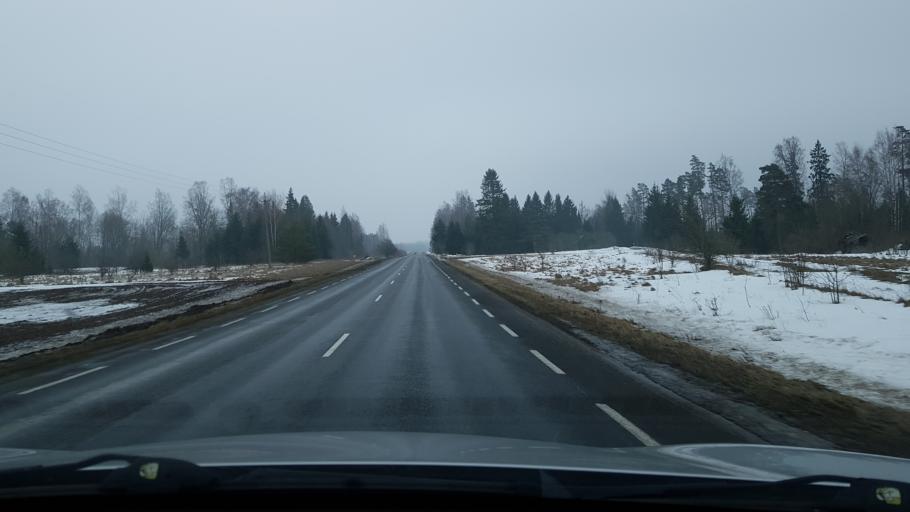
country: EE
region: Viljandimaa
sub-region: Viiratsi vald
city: Viiratsi
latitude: 58.2504
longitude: 25.7569
